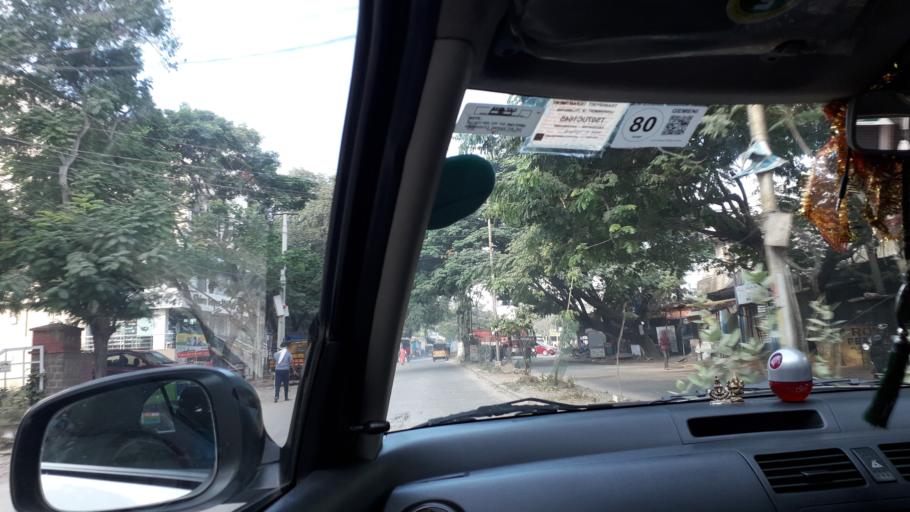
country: IN
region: Telangana
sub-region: Hyderabad
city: Hyderabad
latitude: 17.3934
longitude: 78.3773
